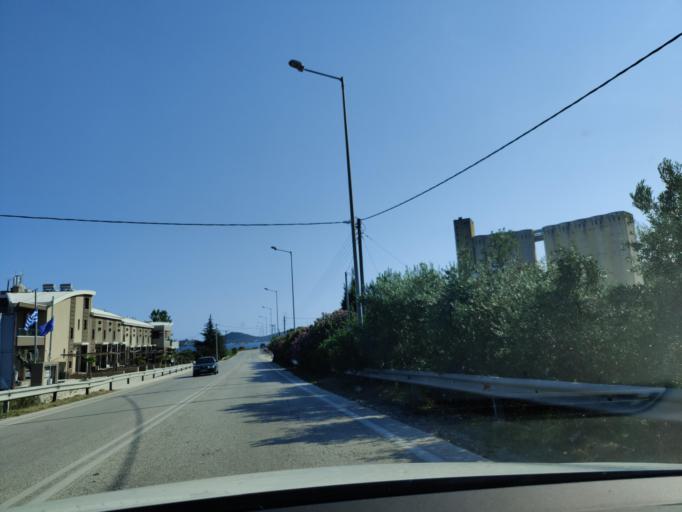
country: GR
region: East Macedonia and Thrace
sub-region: Nomos Kavalas
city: Nea Iraklitsa
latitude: 40.8531
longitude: 24.3137
